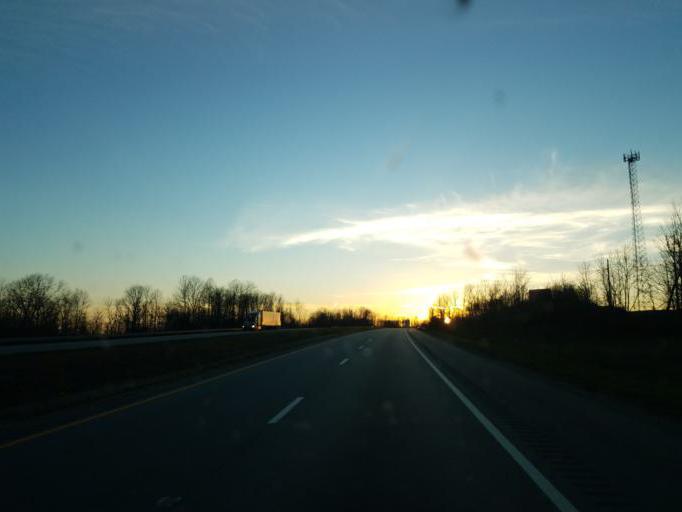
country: US
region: Ohio
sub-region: Belmont County
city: Barnesville
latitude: 40.0563
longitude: -81.2825
